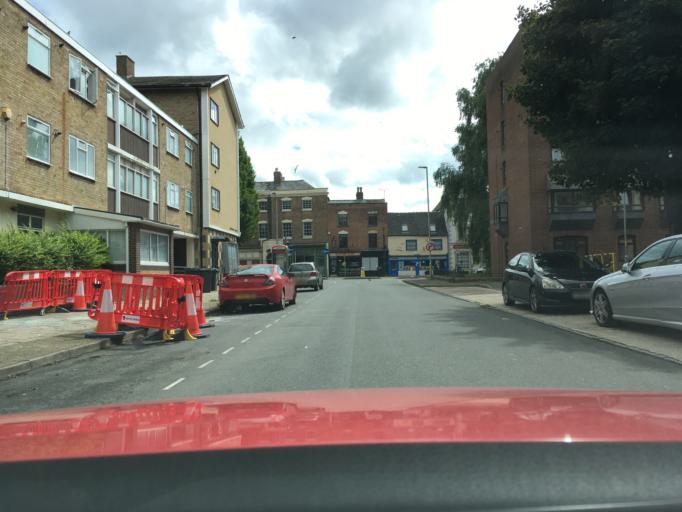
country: GB
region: England
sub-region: Gloucestershire
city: Gloucester
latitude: 51.8680
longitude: -2.2502
